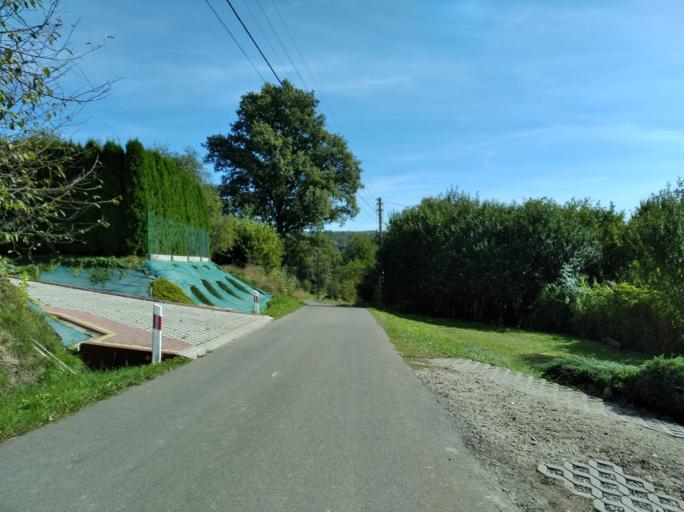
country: PL
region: Subcarpathian Voivodeship
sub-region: Powiat strzyzowski
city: Wisniowa
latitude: 49.8939
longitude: 21.6386
